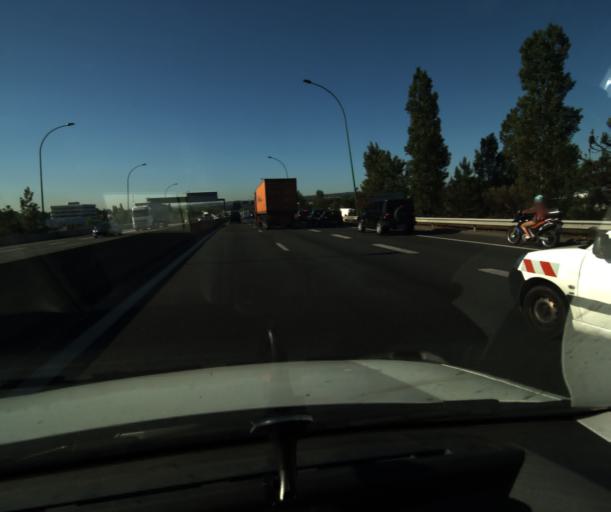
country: FR
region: Midi-Pyrenees
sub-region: Departement de la Haute-Garonne
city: Ramonville-Saint-Agne
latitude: 43.5646
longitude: 1.4936
